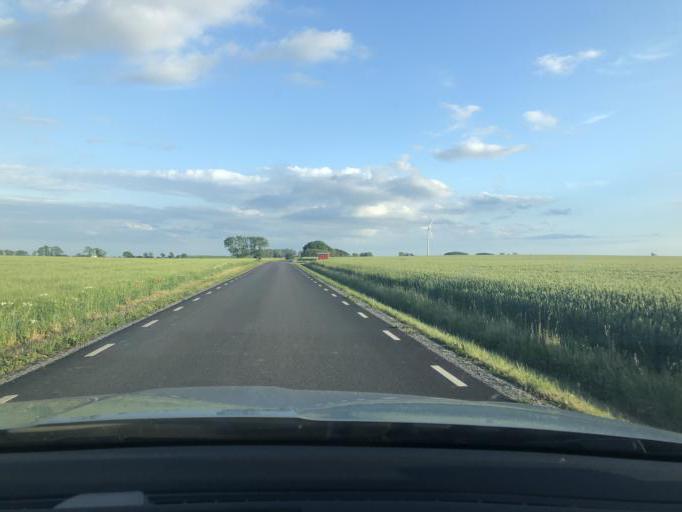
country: SE
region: Skane
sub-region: Simrishamns Kommun
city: Simrishamn
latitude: 55.4819
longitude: 14.1952
